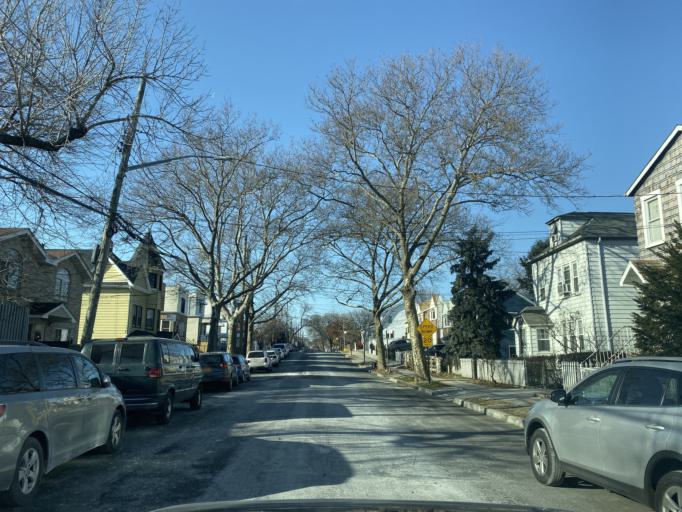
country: US
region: New York
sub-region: Bronx
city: The Bronx
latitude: 40.8262
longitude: -73.8444
